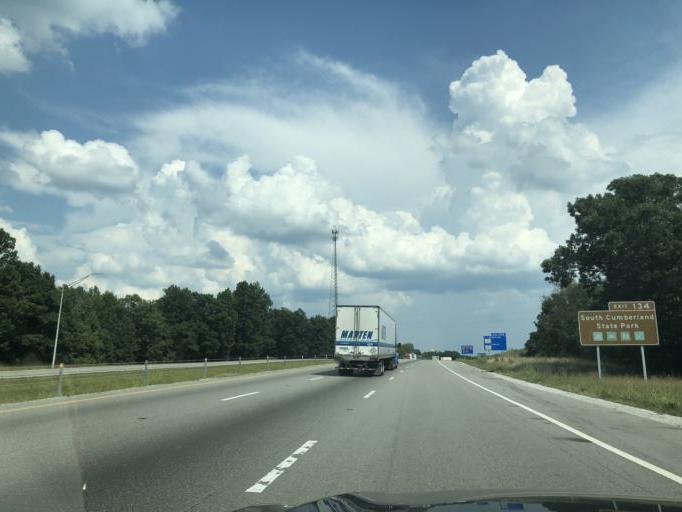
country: US
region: Tennessee
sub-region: Marion County
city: Monteagle
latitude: 35.2431
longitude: -85.8558
